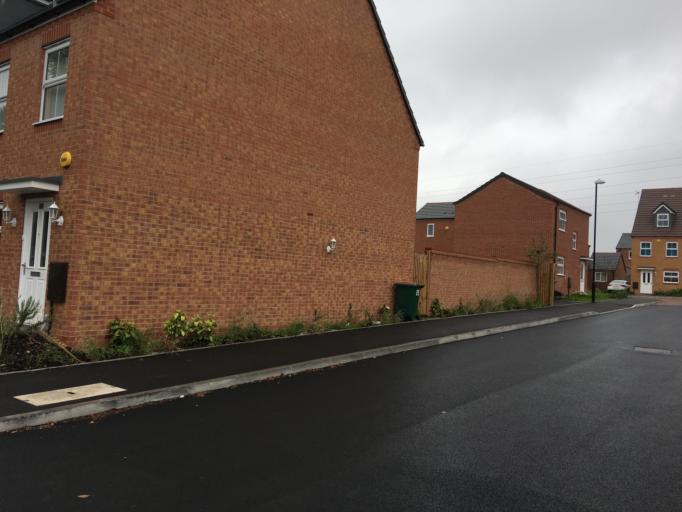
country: GB
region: England
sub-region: Coventry
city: Coventry
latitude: 52.3963
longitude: -1.5579
